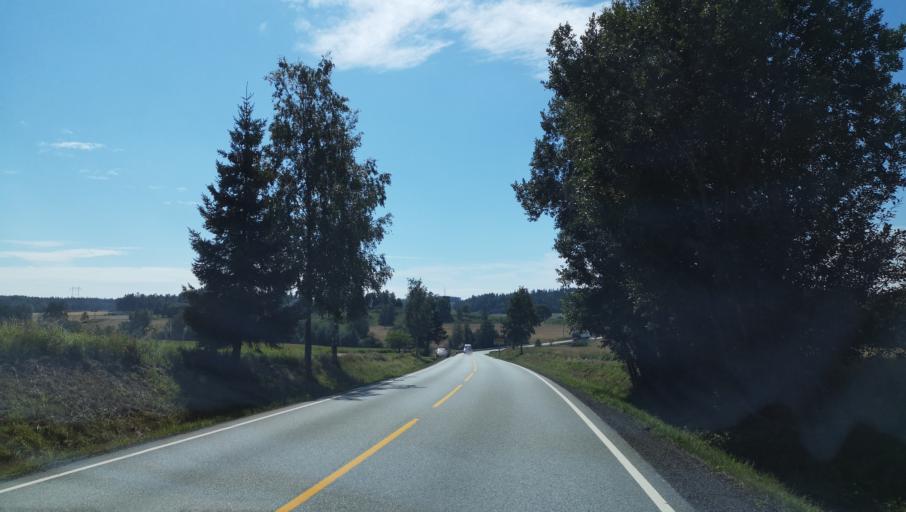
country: NO
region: Akershus
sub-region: Vestby
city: Vestby
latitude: 59.5337
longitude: 10.7561
